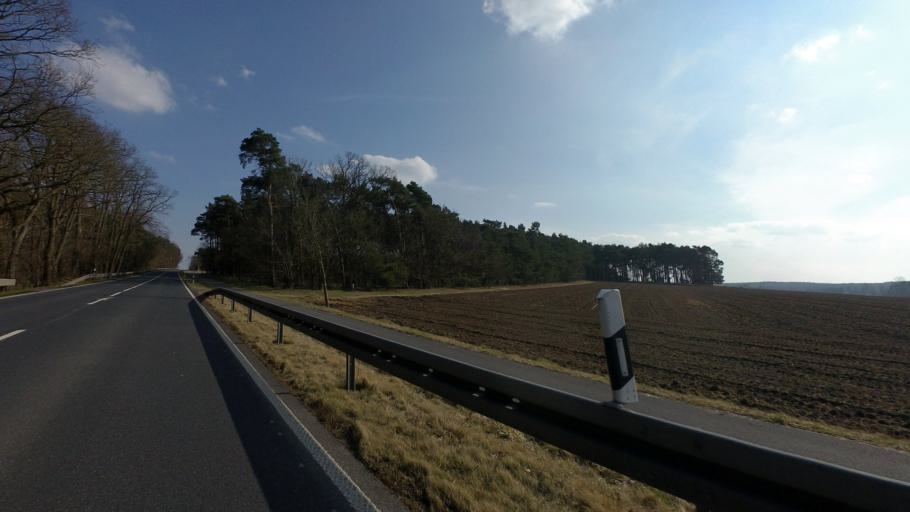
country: DE
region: Brandenburg
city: Beelitz
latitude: 52.2250
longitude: 13.0390
